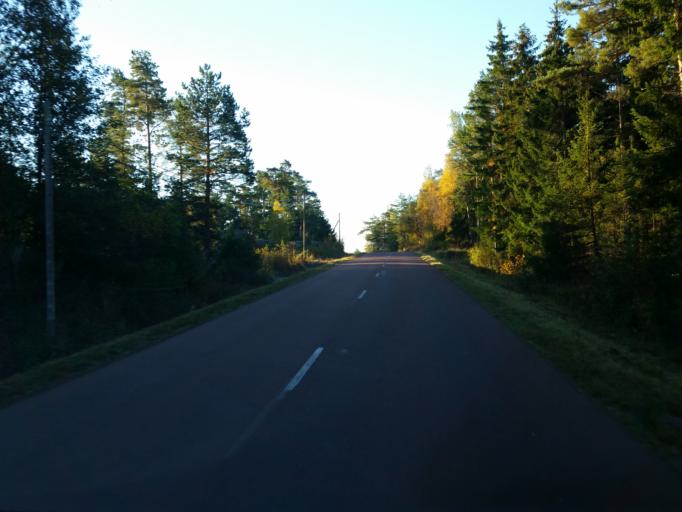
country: AX
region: Alands skaergard
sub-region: Vardoe
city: Vardoe
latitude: 60.2524
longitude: 20.3708
